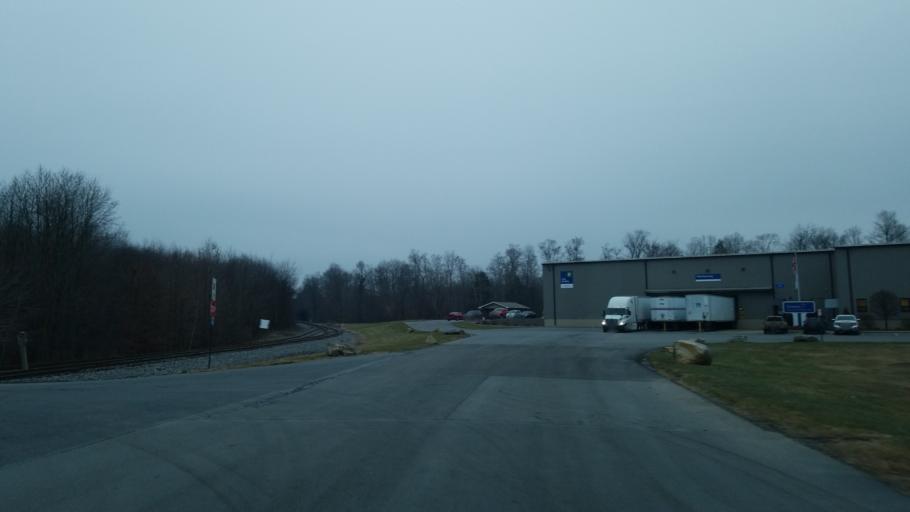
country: US
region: Pennsylvania
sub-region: Clearfield County
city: DuBois
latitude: 41.1164
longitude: -78.7278
